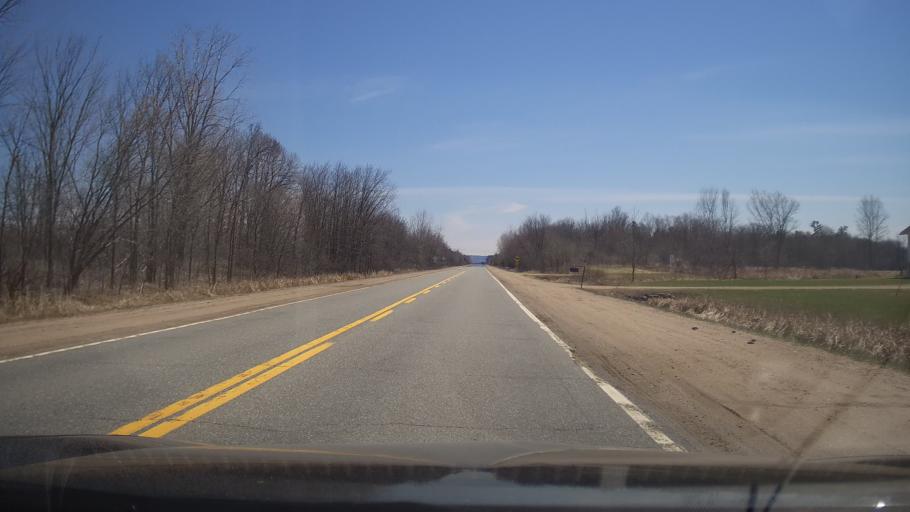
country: CA
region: Ontario
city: Arnprior
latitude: 45.5274
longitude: -76.2232
